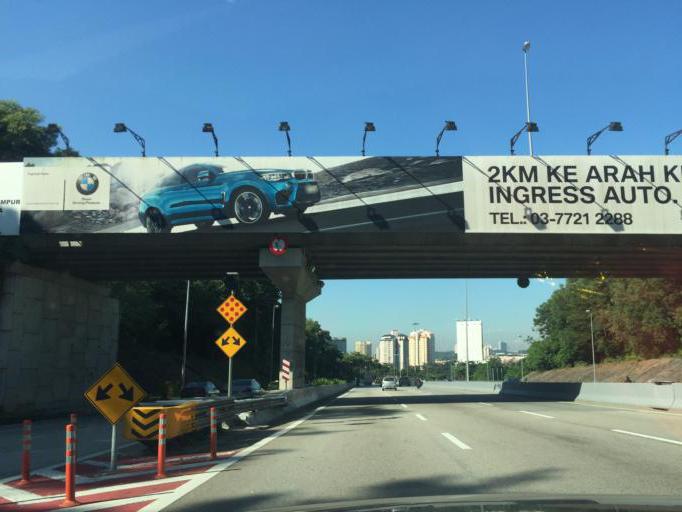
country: MY
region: Kuala Lumpur
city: Kuala Lumpur
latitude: 3.1626
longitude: 101.6305
